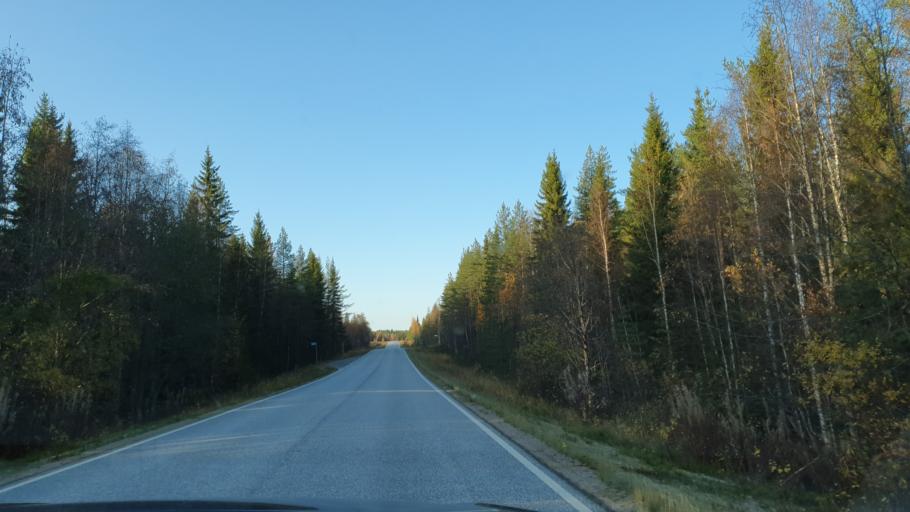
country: FI
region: Kainuu
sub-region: Kehys-Kainuu
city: Kuhmo
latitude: 64.3833
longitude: 29.4737
